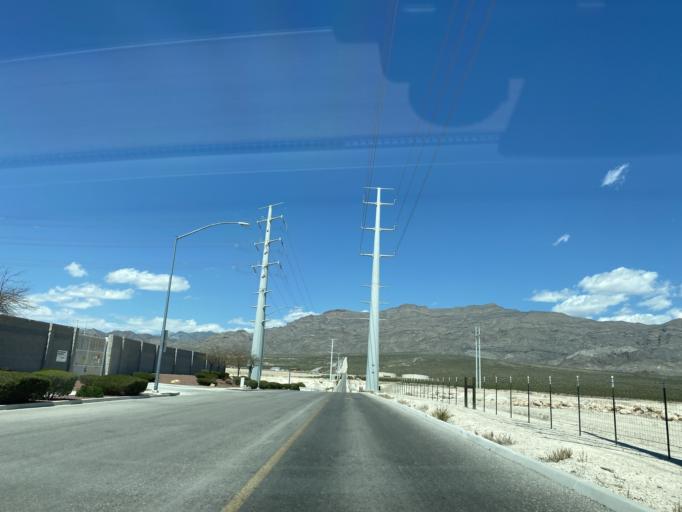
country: US
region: Nevada
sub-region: Clark County
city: North Las Vegas
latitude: 36.3231
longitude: -115.2071
